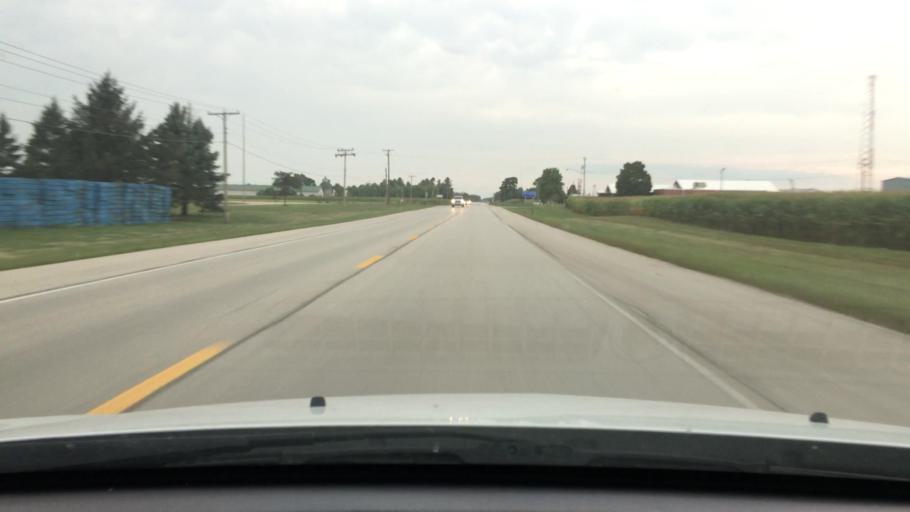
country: US
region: Illinois
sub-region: DeKalb County
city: DeKalb
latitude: 41.8765
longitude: -88.7538
